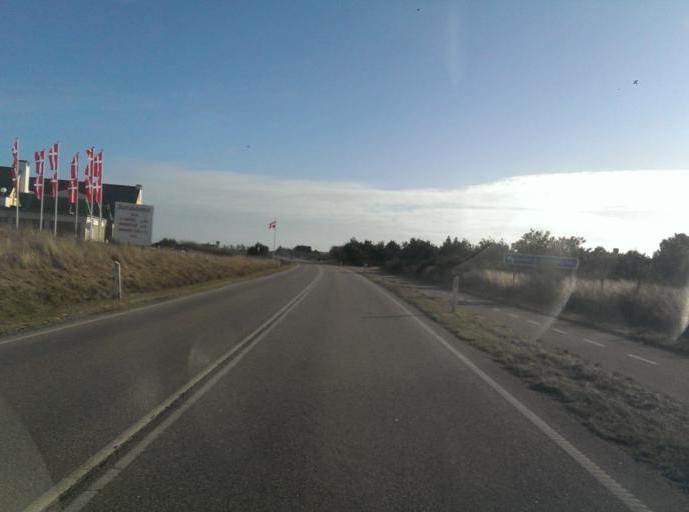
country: DK
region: Central Jutland
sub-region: Ringkobing-Skjern Kommune
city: Hvide Sande
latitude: 56.0538
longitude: 8.1197
